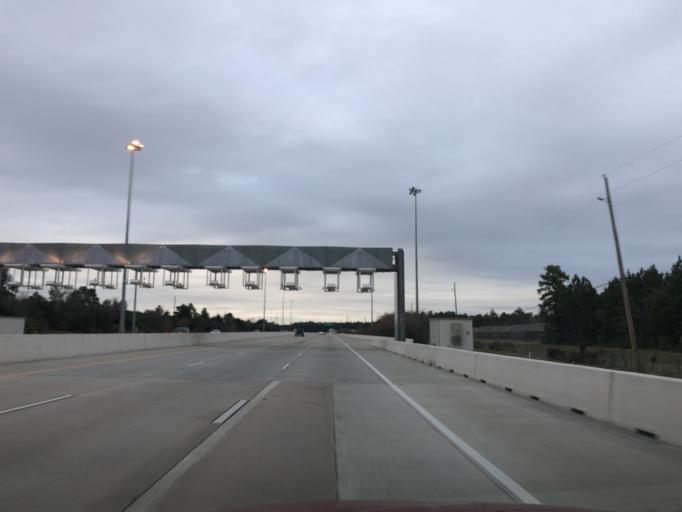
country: US
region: Texas
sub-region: Harris County
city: Spring
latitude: 30.0561
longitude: -95.4043
